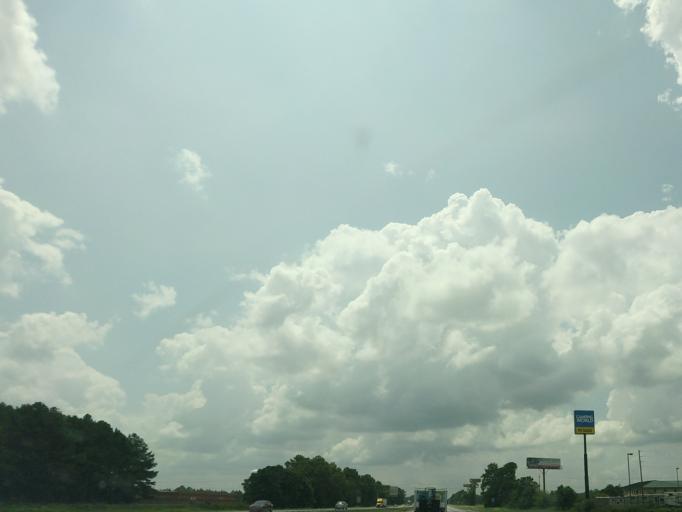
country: US
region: Georgia
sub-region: Peach County
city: Byron
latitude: 32.6529
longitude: -83.7441
